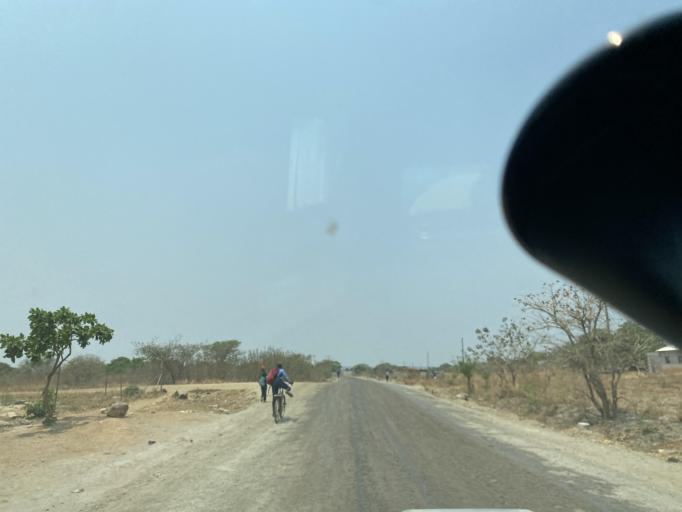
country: ZM
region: Lusaka
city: Lusaka
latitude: -15.5612
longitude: 28.4205
